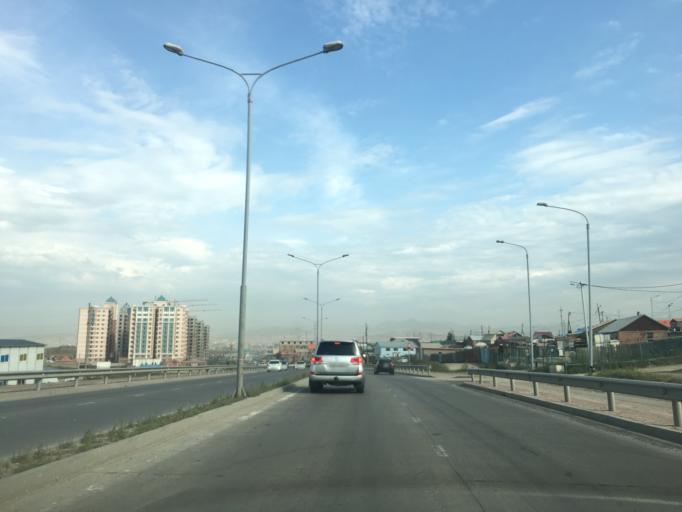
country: MN
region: Ulaanbaatar
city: Ulaanbaatar
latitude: 47.8638
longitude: 106.7881
